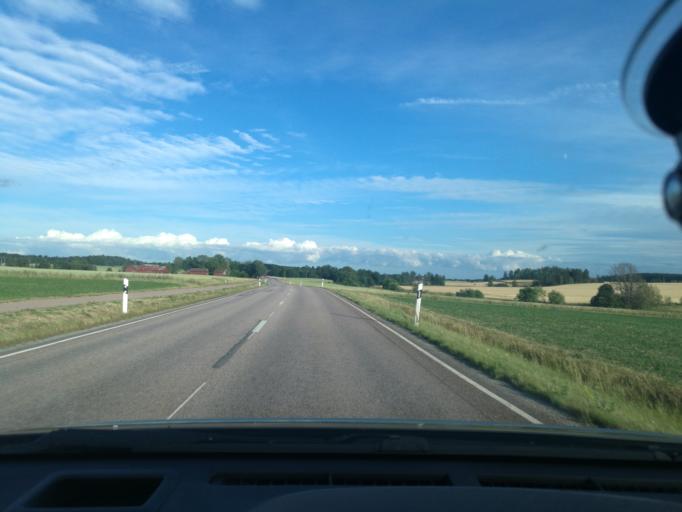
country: SE
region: Vaestmanland
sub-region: Vasteras
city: Skultuna
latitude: 59.6895
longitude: 16.4443
